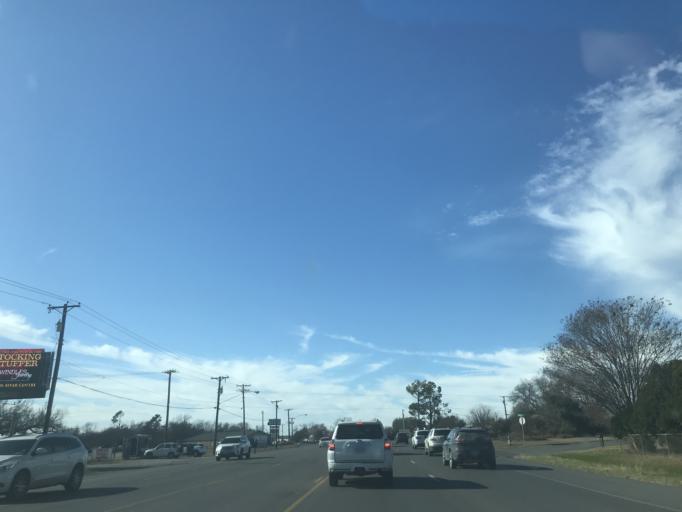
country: US
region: Texas
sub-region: Erath County
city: Stephenville
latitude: 32.2068
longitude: -98.2223
